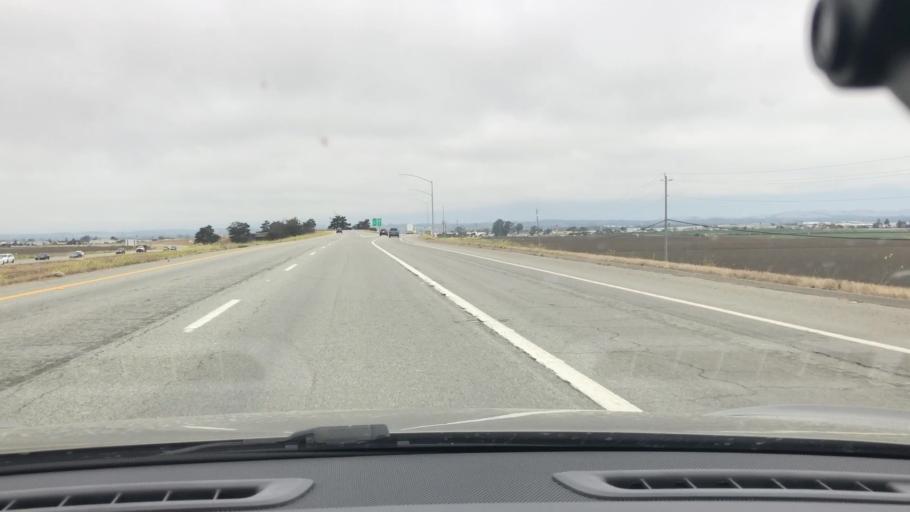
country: US
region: California
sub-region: Monterey County
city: Castroville
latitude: 36.7495
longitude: -121.7716
